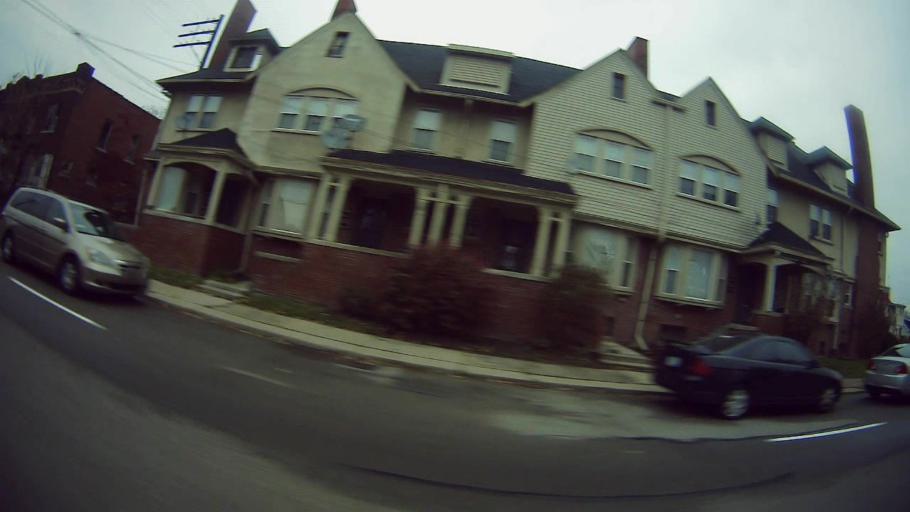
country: US
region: Michigan
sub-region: Wayne County
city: Hamtramck
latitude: 42.3752
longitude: -83.0738
